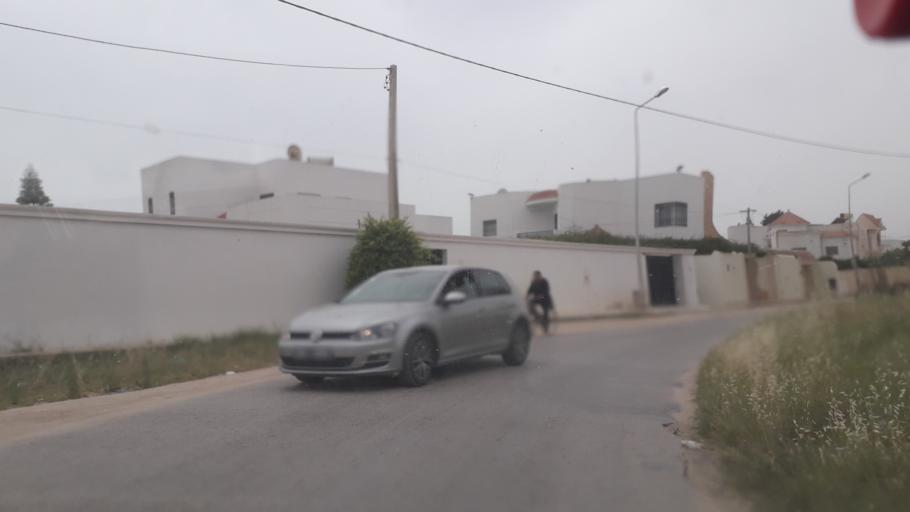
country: TN
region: Safaqis
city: Al Qarmadah
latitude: 34.7923
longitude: 10.7636
